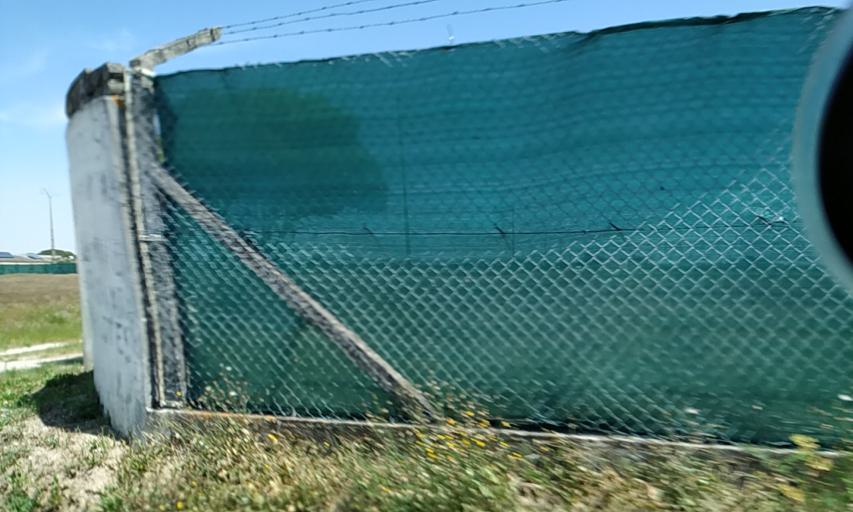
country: PT
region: Santarem
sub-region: Benavente
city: Poceirao
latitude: 38.6677
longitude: -8.7366
